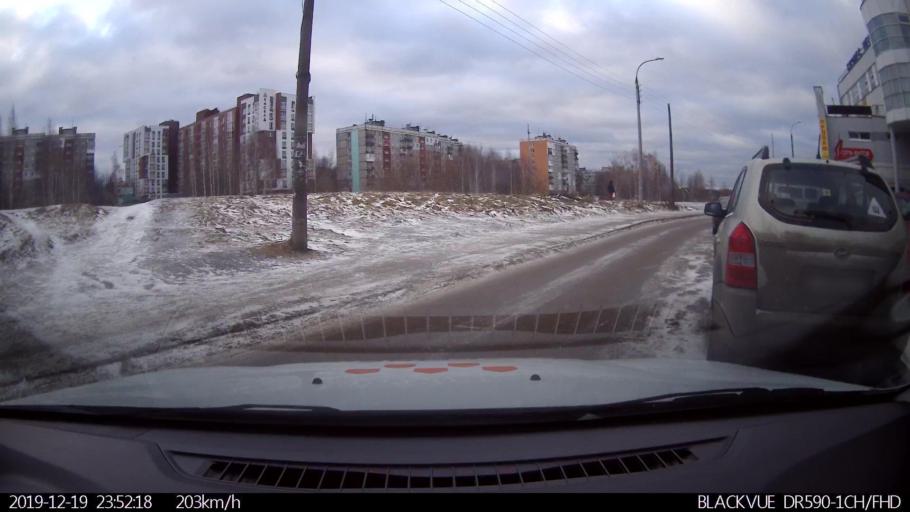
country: RU
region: Vologda
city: Molochnoye
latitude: 58.9944
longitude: 39.4861
